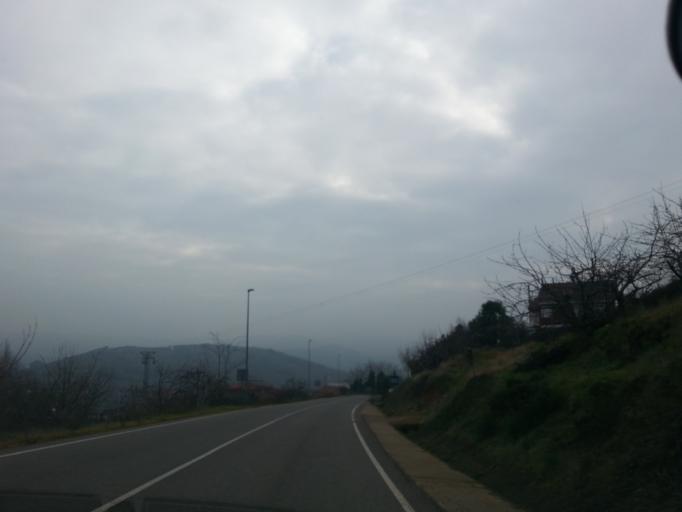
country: ES
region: Castille and Leon
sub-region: Provincia de Salamanca
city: Sotoserrano
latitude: 40.4388
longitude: -6.0369
